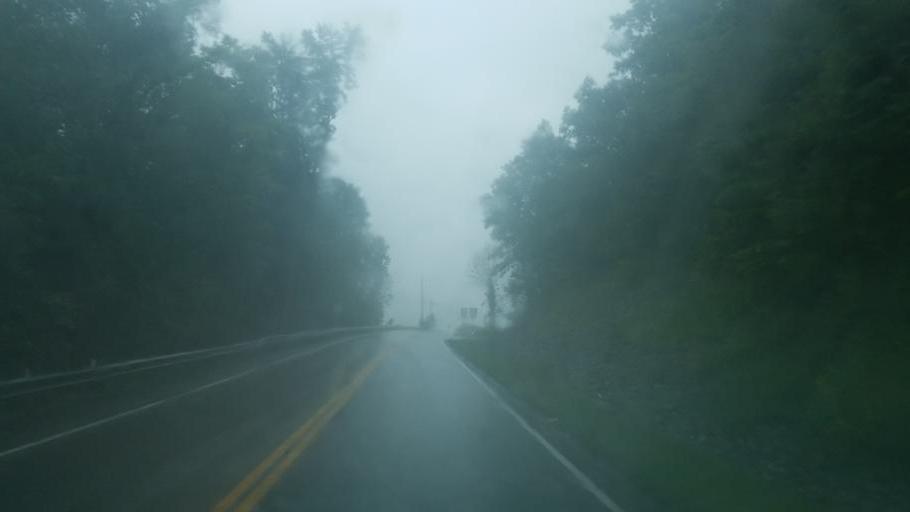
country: US
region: Kentucky
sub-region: Rowan County
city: Morehead
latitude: 38.2556
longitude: -83.5263
